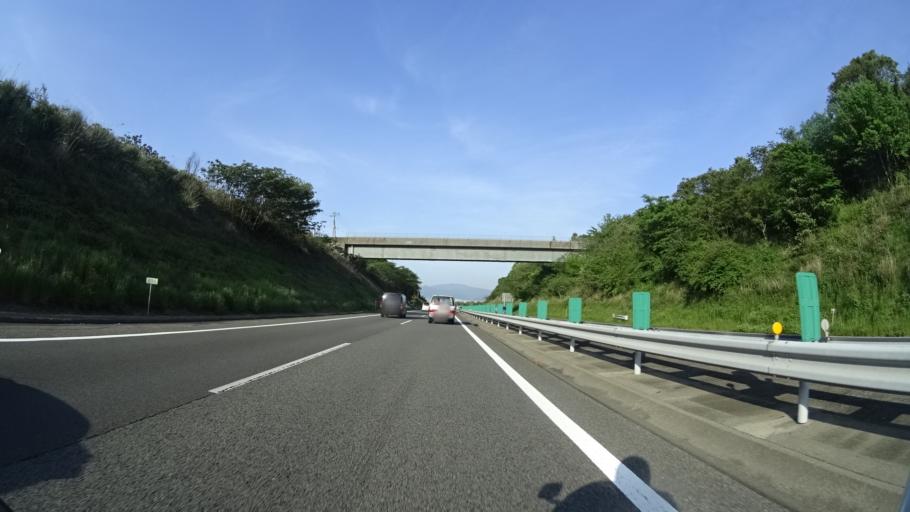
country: JP
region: Ehime
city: Kawanoecho
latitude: 33.9578
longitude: 133.4766
